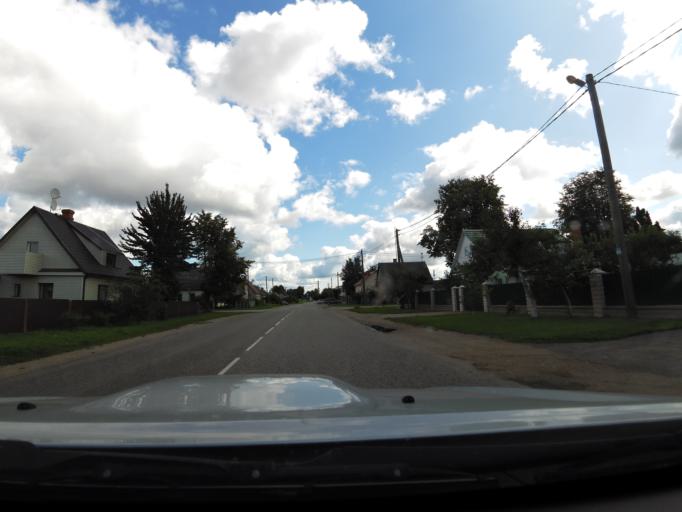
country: LV
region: Daugavpils
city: Daugavpils
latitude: 55.8648
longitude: 26.4959
